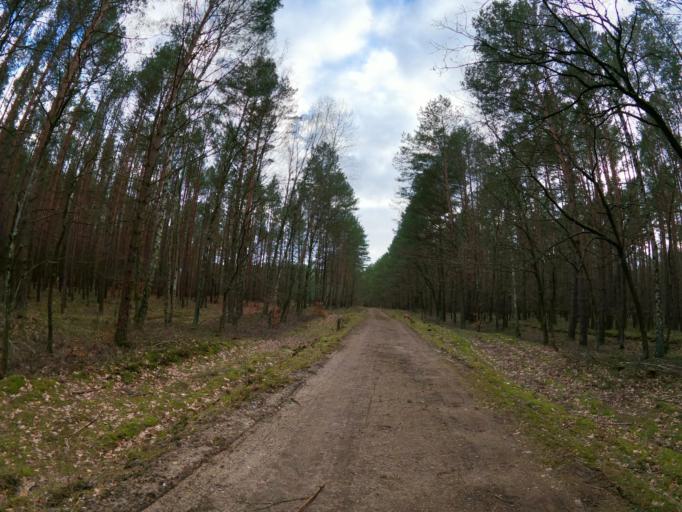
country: PL
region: West Pomeranian Voivodeship
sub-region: Powiat kamienski
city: Golczewo
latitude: 53.8443
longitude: 15.0078
